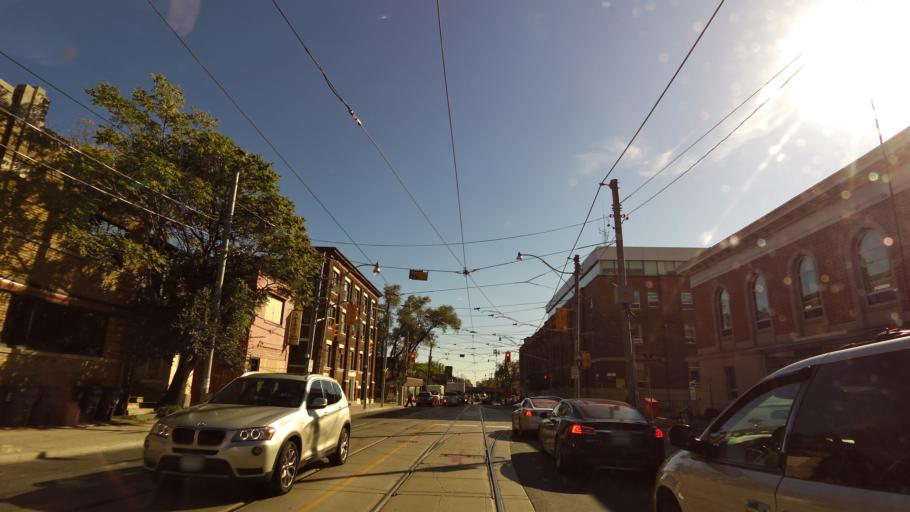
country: CA
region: Ontario
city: Toronto
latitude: 43.6756
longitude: -79.4153
